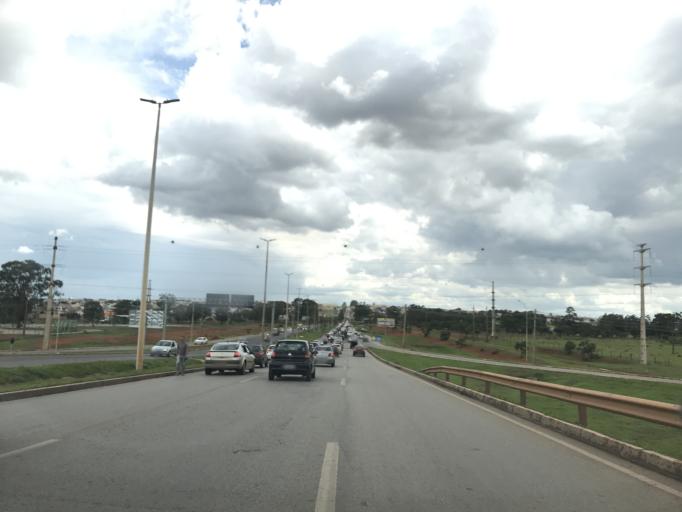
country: BR
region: Federal District
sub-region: Brasilia
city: Brasilia
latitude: -15.8835
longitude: -48.0601
